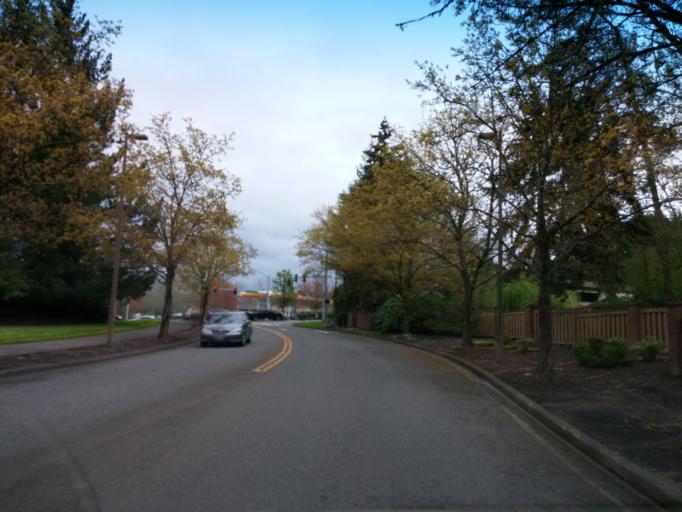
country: US
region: Oregon
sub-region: Washington County
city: Oak Hills
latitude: 45.5285
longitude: -122.8409
